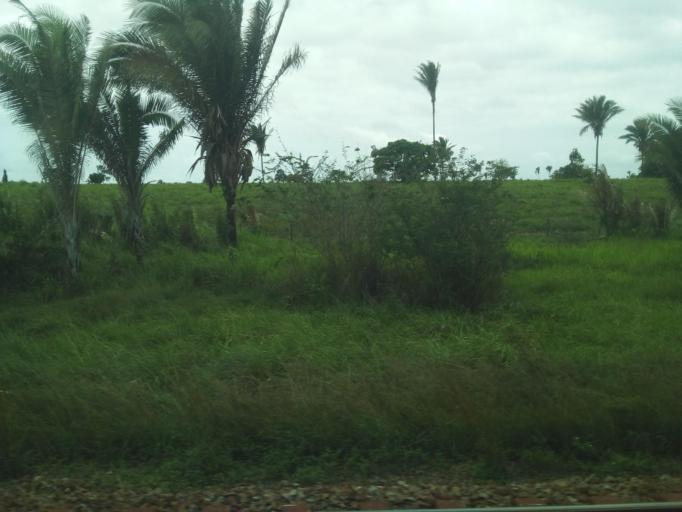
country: BR
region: Maranhao
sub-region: Santa Ines
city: Santa Ines
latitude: -3.6835
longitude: -45.3418
